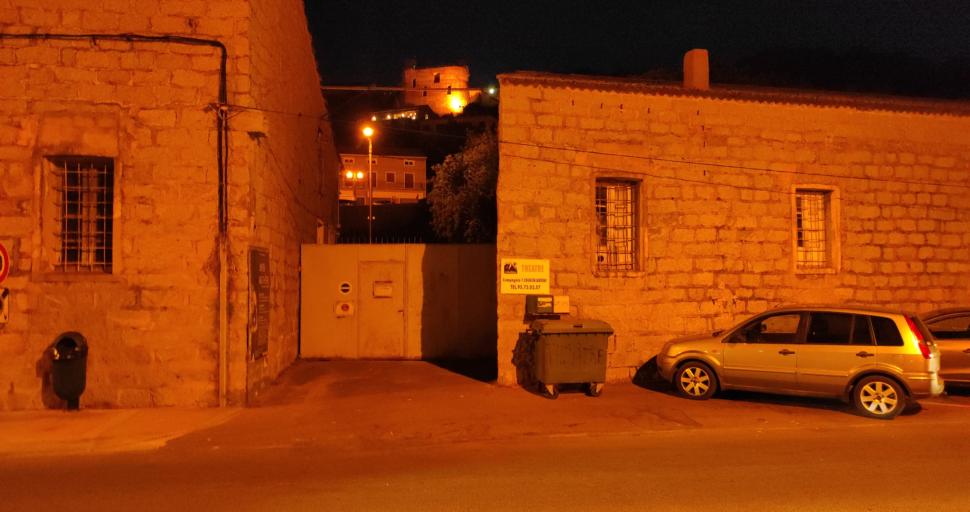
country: FR
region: Corsica
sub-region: Departement de la Corse-du-Sud
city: Porto-Vecchio
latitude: 41.5913
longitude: 9.2834
